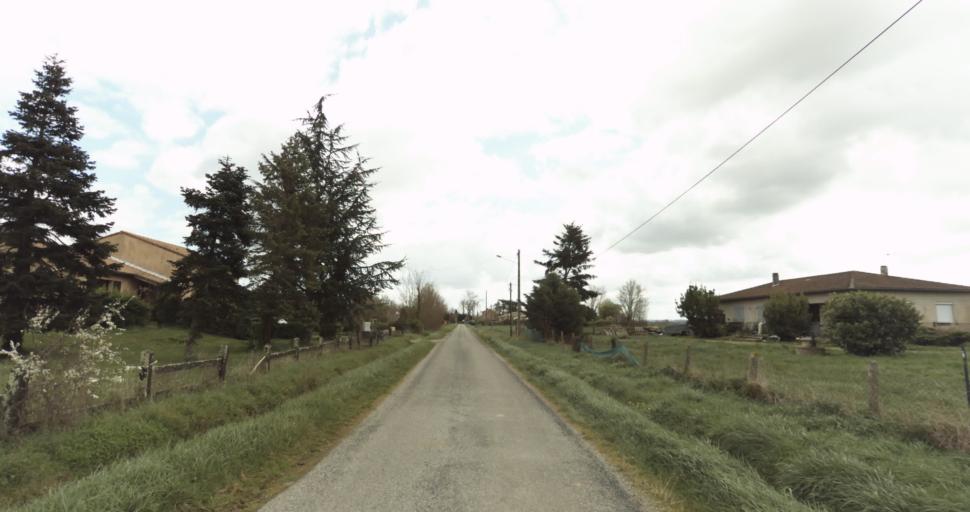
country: FR
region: Midi-Pyrenees
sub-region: Departement de la Haute-Garonne
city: Auterive
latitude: 43.3275
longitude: 1.4676
